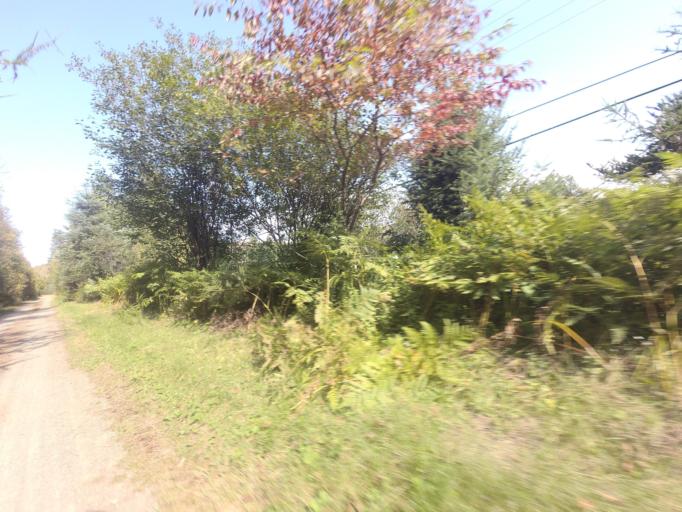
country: CA
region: Quebec
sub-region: Laurentides
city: Sainte-Agathe-des-Monts
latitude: 46.0745
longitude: -74.3160
